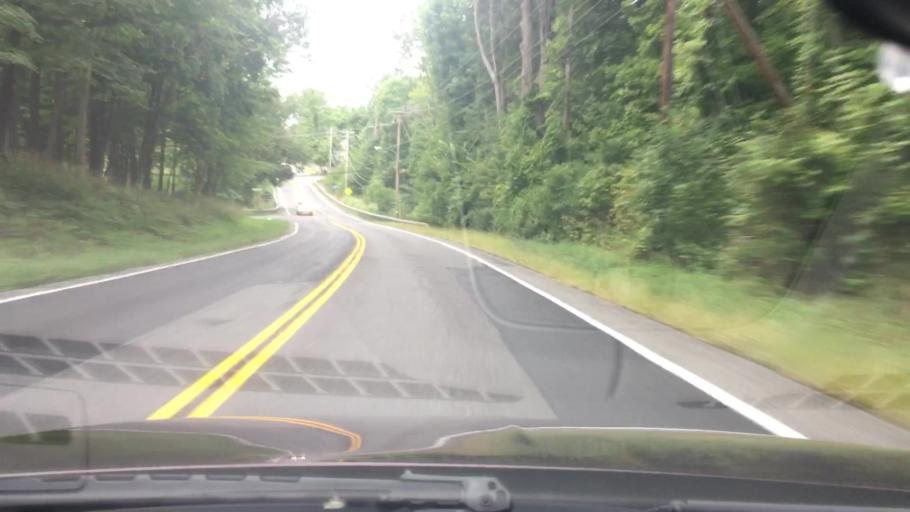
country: US
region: New York
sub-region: Dutchess County
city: Millbrook
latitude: 41.7935
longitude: -73.6921
